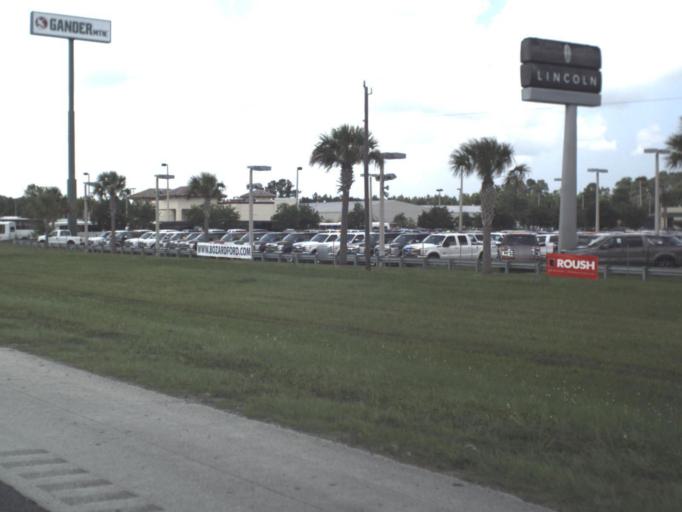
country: US
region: Florida
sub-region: Saint Johns County
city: Saint Augustine
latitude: 29.9261
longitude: -81.4165
